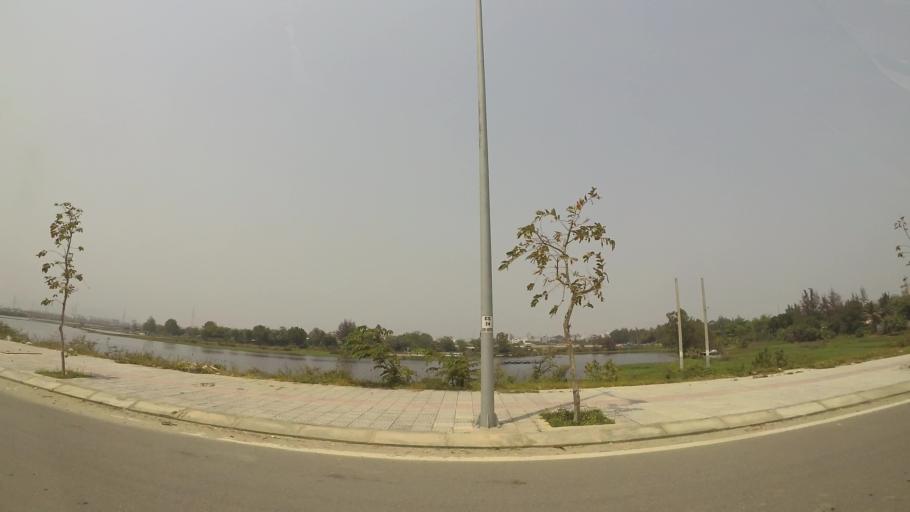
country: VN
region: Da Nang
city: Ngu Hanh Son
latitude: 16.0131
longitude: 108.2491
